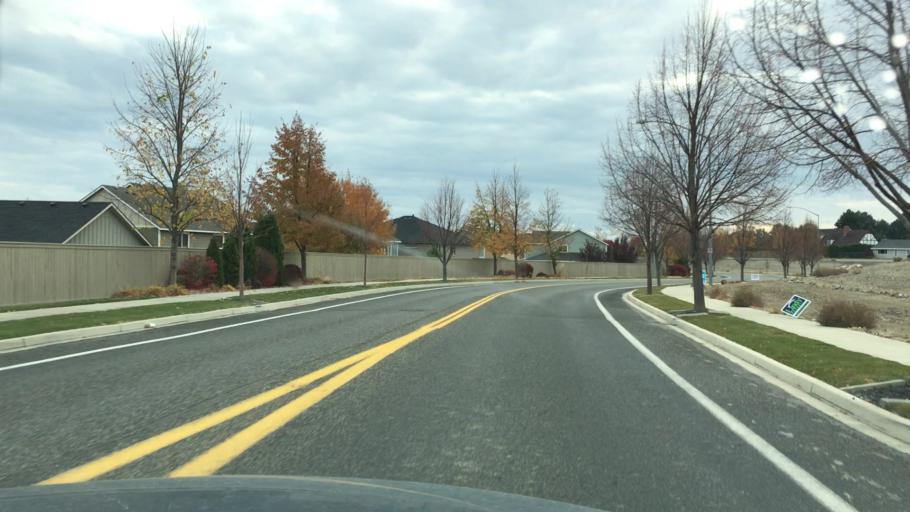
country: US
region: Washington
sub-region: Franklin County
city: West Pasco
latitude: 46.1887
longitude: -119.1956
